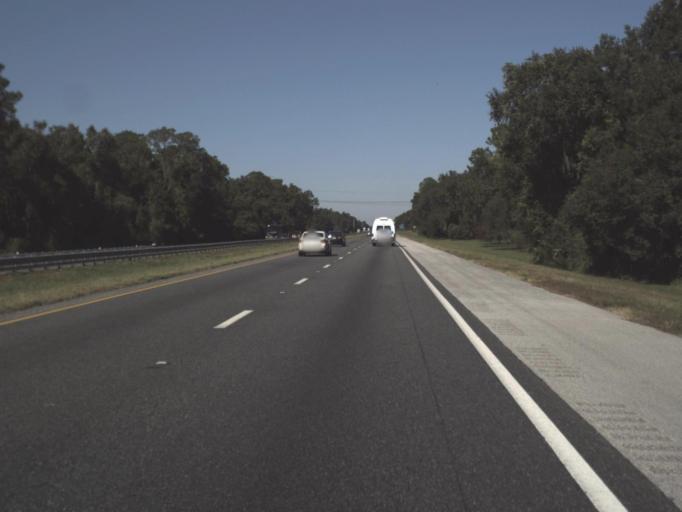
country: US
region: Florida
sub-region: Sumter County
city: Wildwood
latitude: 28.8097
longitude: -82.0096
